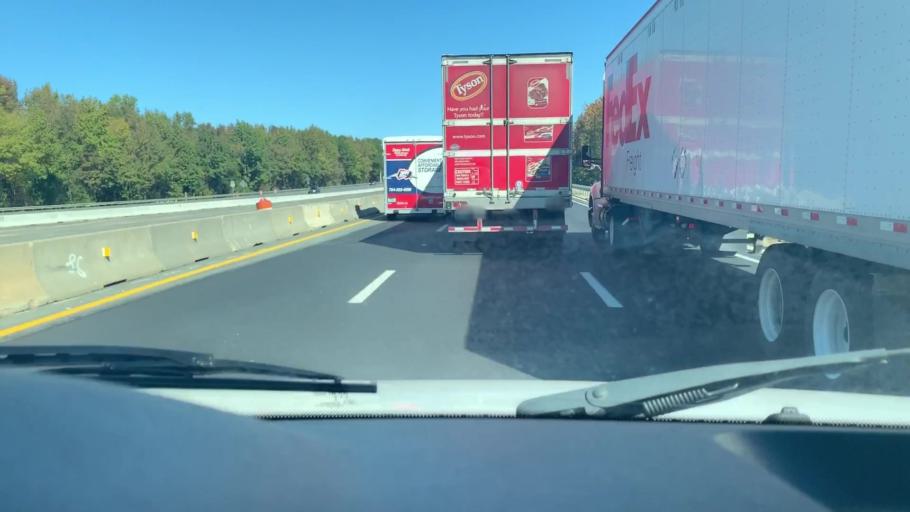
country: US
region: North Carolina
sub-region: Mecklenburg County
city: Huntersville
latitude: 35.3402
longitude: -80.8484
